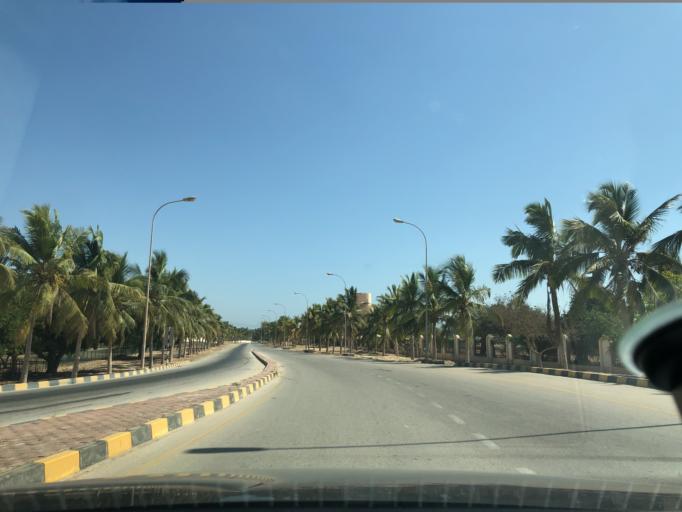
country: OM
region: Zufar
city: Salalah
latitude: 17.0399
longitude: 54.3741
